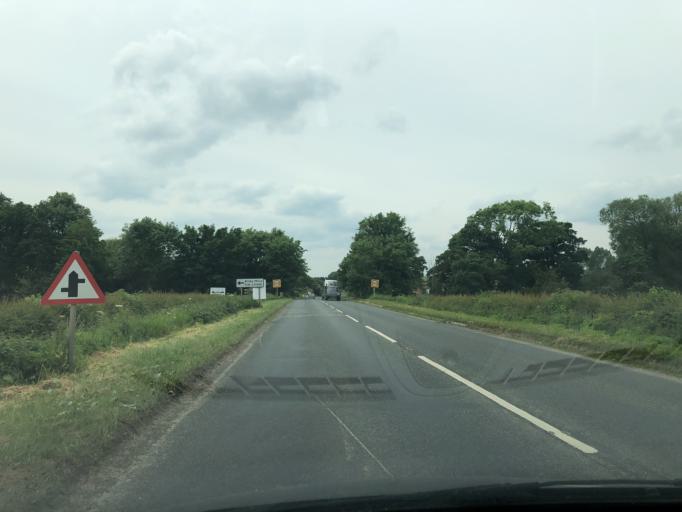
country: GB
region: England
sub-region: North Yorkshire
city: Great Habton
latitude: 54.2641
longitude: -0.9173
